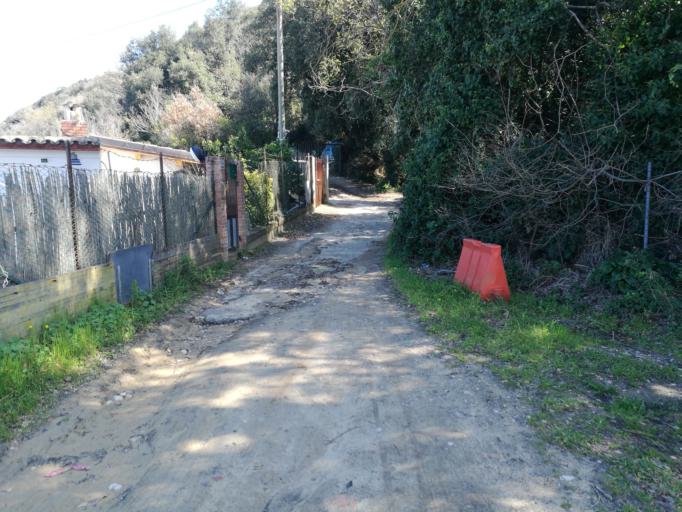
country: IT
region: Molise
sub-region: Provincia di Campobasso
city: Termoli
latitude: 41.9845
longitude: 14.9782
